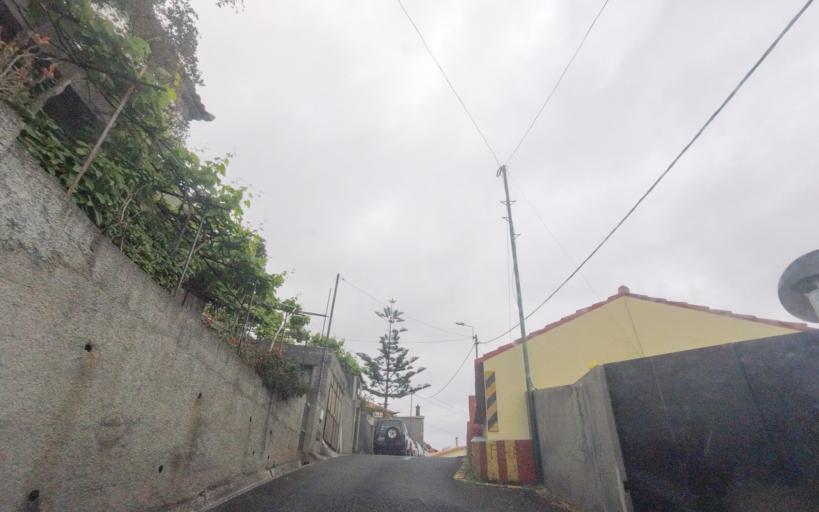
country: PT
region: Madeira
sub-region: Funchal
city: Nossa Senhora do Monte
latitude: 32.6642
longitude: -16.9139
